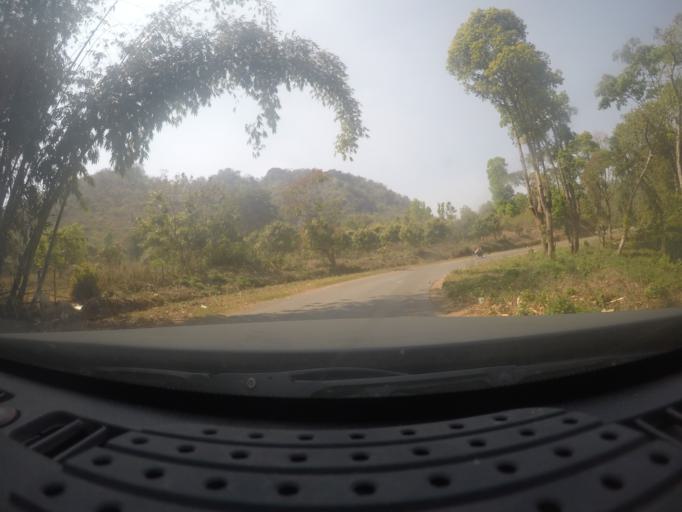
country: MM
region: Mandalay
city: Kyaukse
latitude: 21.1356
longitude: 96.4502
